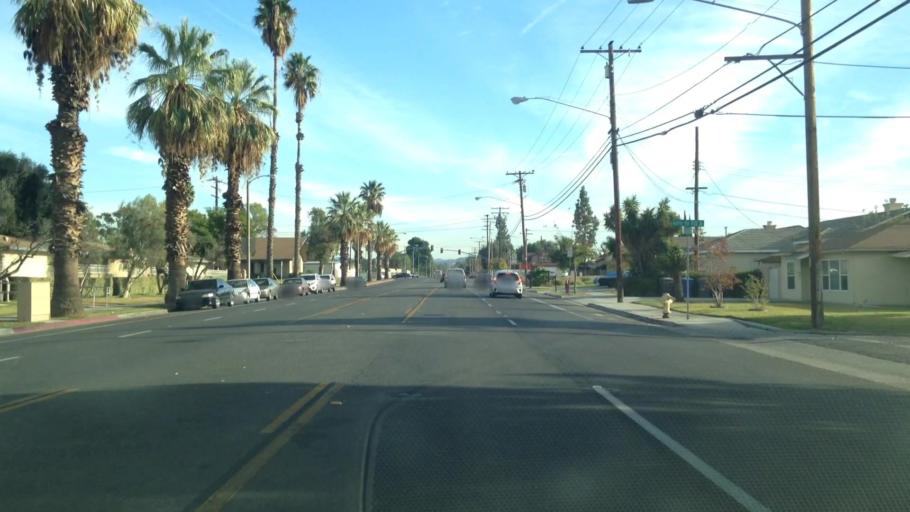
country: US
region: California
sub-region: Riverside County
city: Pedley
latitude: 33.9387
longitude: -117.4508
